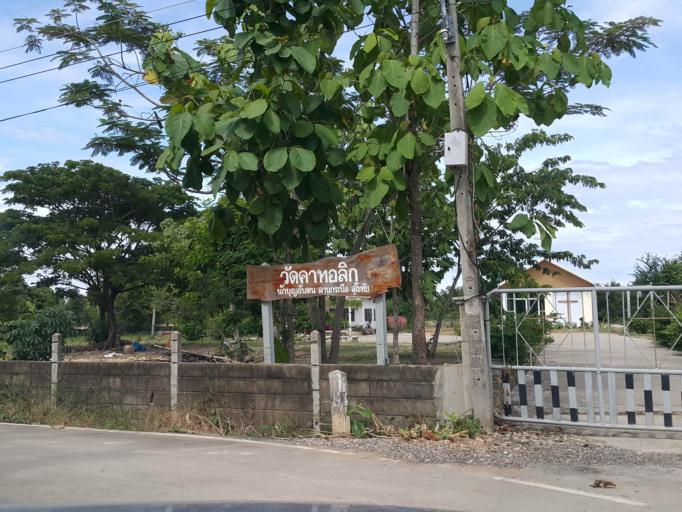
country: TH
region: Sukhothai
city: Ban Dan Lan Hoi
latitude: 17.1083
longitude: 99.4758
